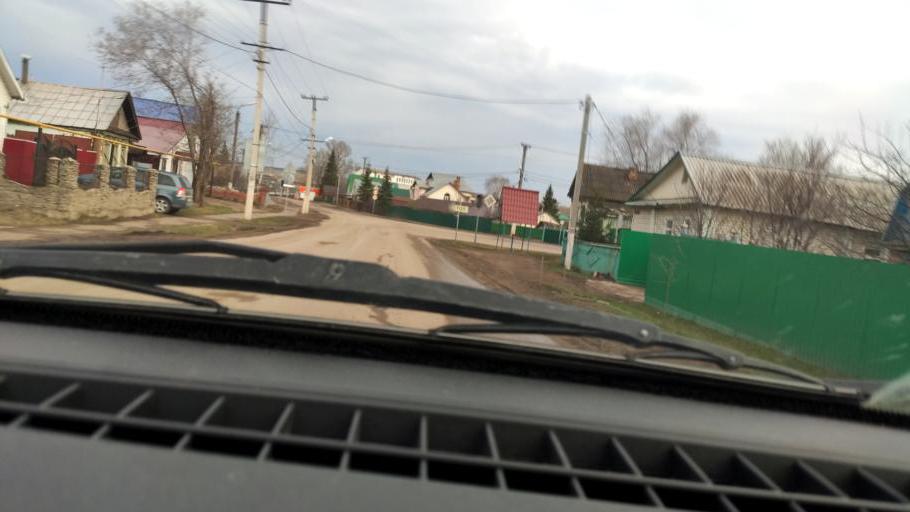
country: RU
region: Bashkortostan
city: Davlekanovo
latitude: 54.2131
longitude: 55.0361
